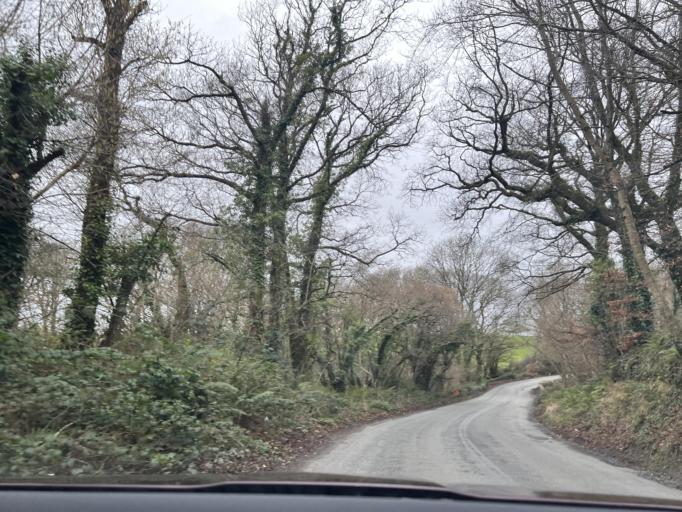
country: IE
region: Leinster
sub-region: Loch Garman
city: Castlebridge
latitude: 52.3799
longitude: -6.5365
